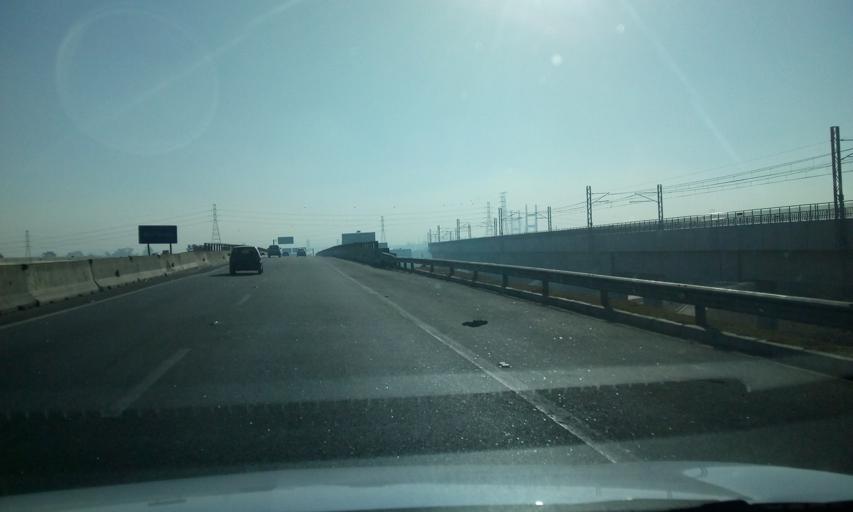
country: BR
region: Sao Paulo
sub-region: Guarulhos
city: Guarulhos
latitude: -23.4784
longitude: -46.5008
